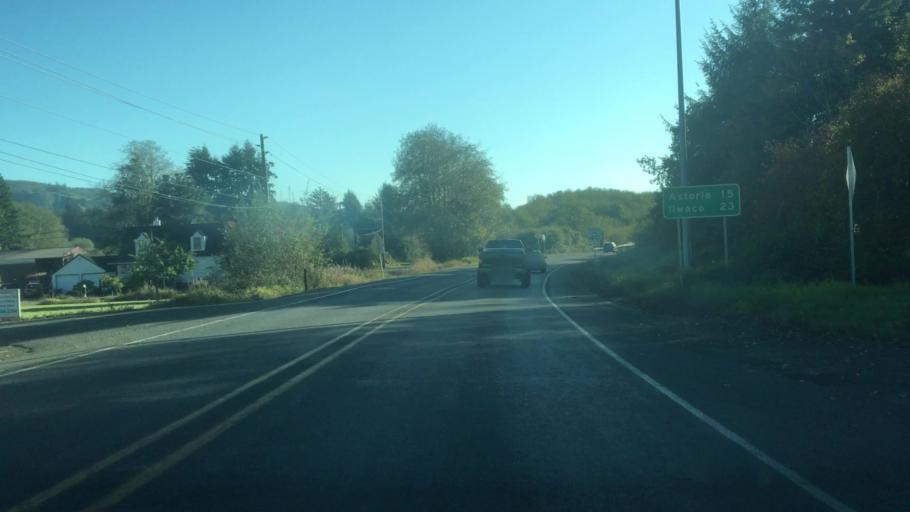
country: US
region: Oregon
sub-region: Clatsop County
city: Astoria
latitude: 46.3754
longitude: -123.8026
